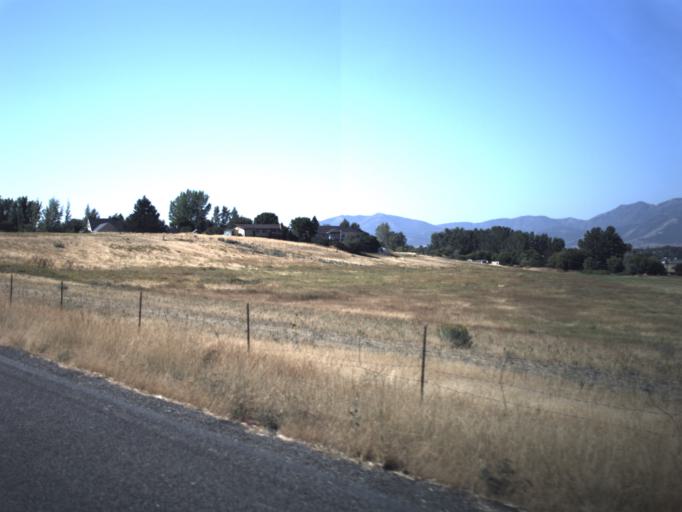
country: US
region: Utah
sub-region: Cache County
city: Hyrum
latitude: 41.6460
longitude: -111.8328
